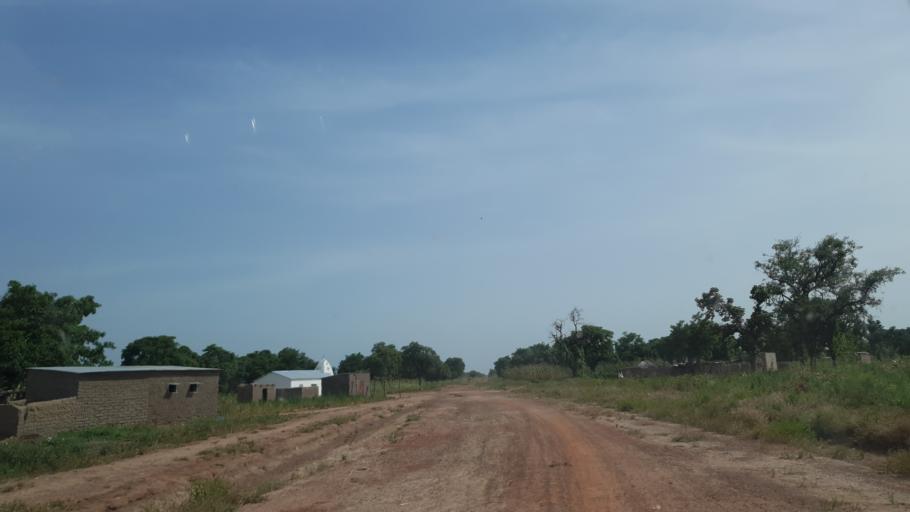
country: ML
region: Koulikoro
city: Dioila
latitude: 12.4256
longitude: -6.2224
